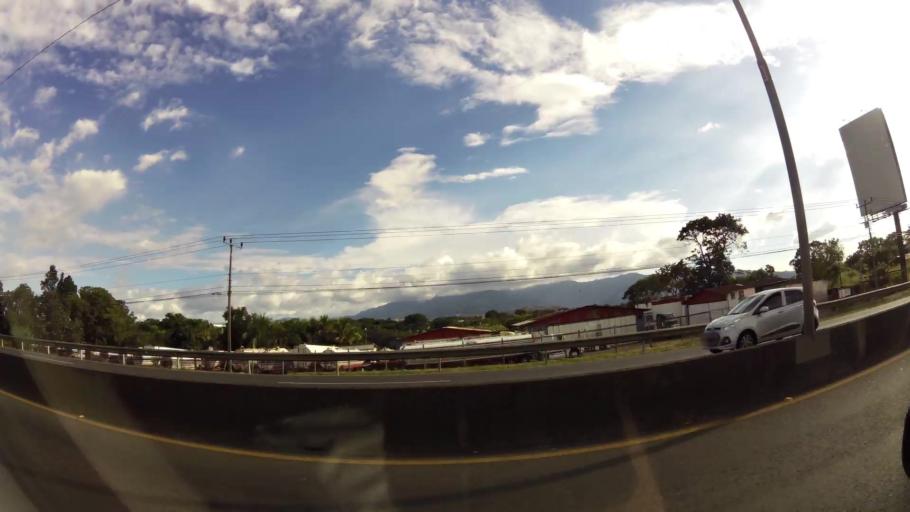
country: CR
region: Heredia
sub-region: Canton de Belen
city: San Antonio
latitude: 10.0018
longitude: -84.1824
